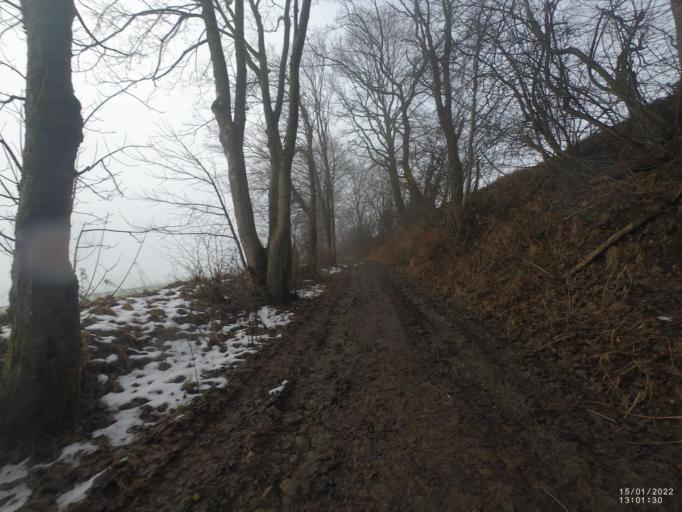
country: DE
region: North Rhine-Westphalia
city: Kierspe
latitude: 51.1115
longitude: 7.6056
